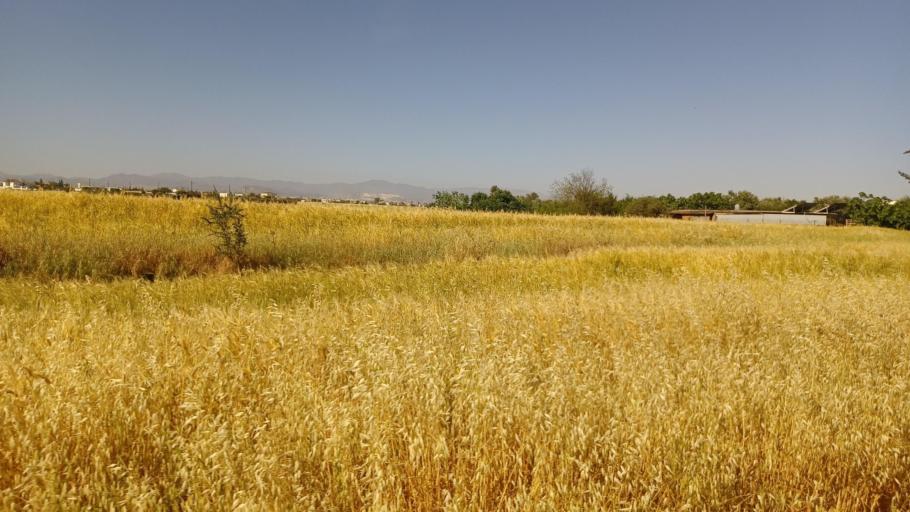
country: CY
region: Lefkosia
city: Kokkinotrimithia
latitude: 35.1434
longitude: 33.2172
